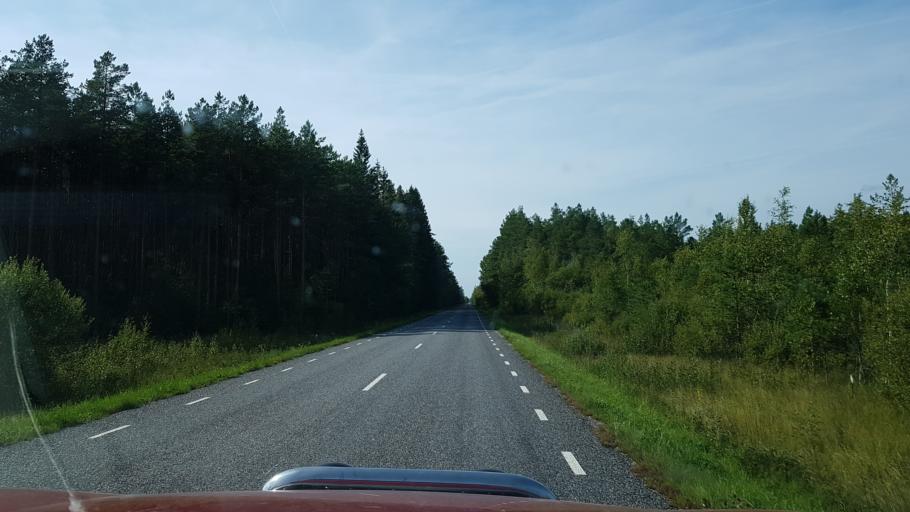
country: EE
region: Paernumaa
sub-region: Saarde vald
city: Kilingi-Nomme
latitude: 58.3525
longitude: 25.1158
